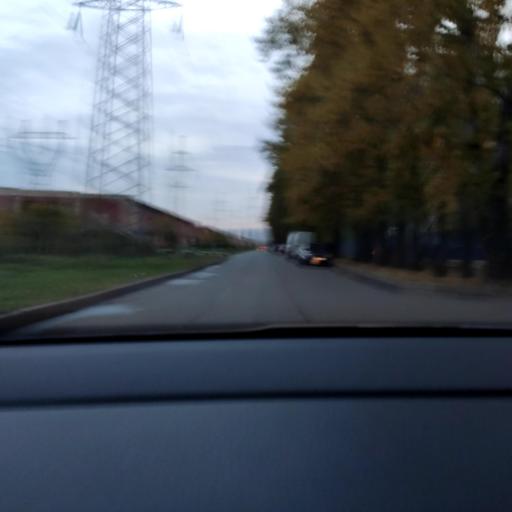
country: RU
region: Moscow
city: Bibirevo
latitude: 55.8878
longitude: 37.6195
